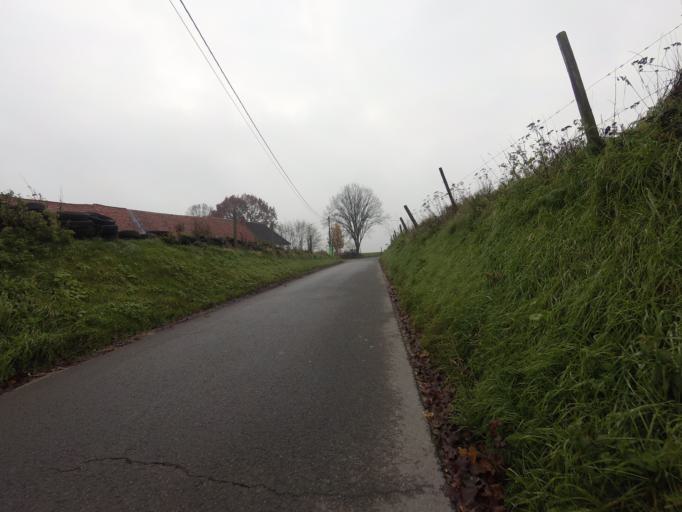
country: BE
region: Flanders
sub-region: Provincie Oost-Vlaanderen
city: Ninove
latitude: 50.8267
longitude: 3.9929
